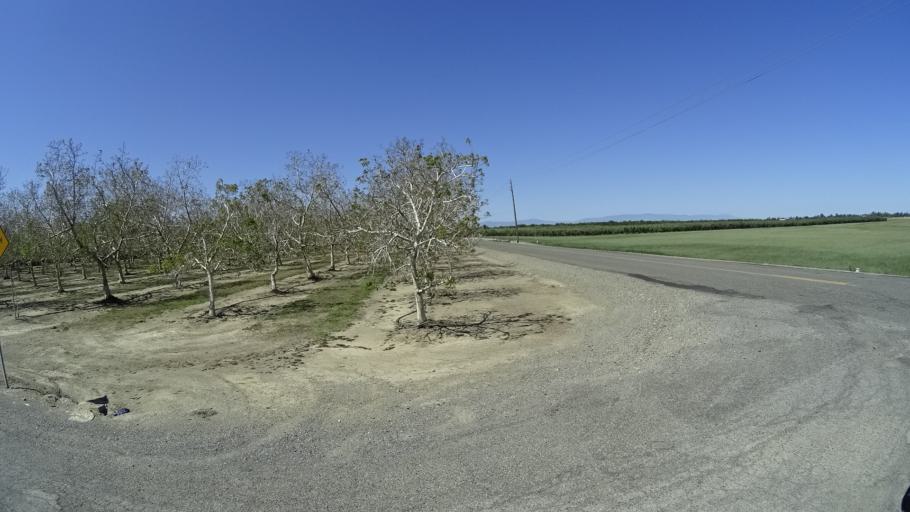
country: US
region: California
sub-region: Glenn County
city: Orland
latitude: 39.7106
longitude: -122.1456
